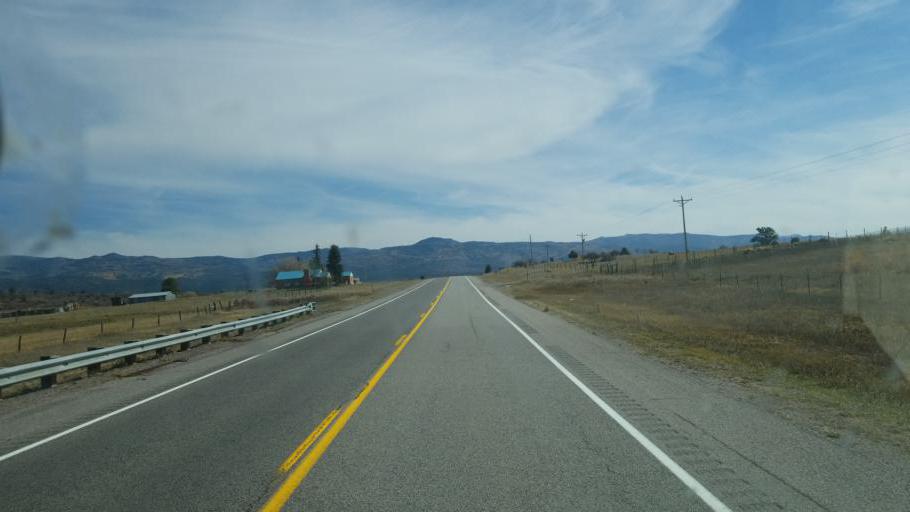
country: US
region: New Mexico
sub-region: Rio Arriba County
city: Chama
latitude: 36.8874
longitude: -106.6215
